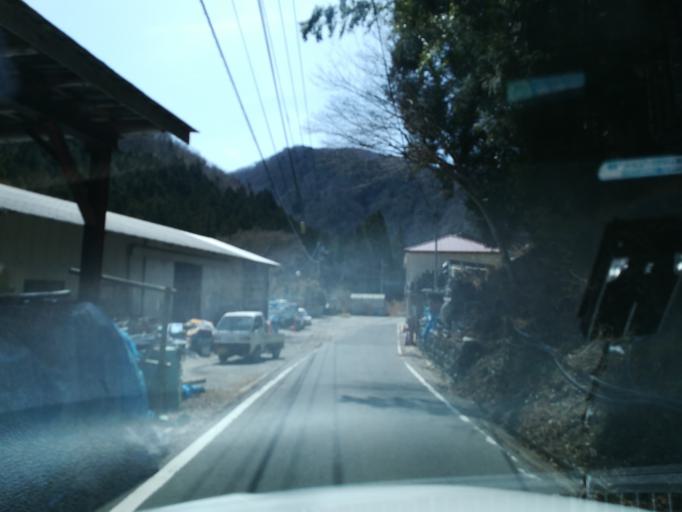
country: JP
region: Tokushima
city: Wakimachi
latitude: 33.8523
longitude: 134.0265
